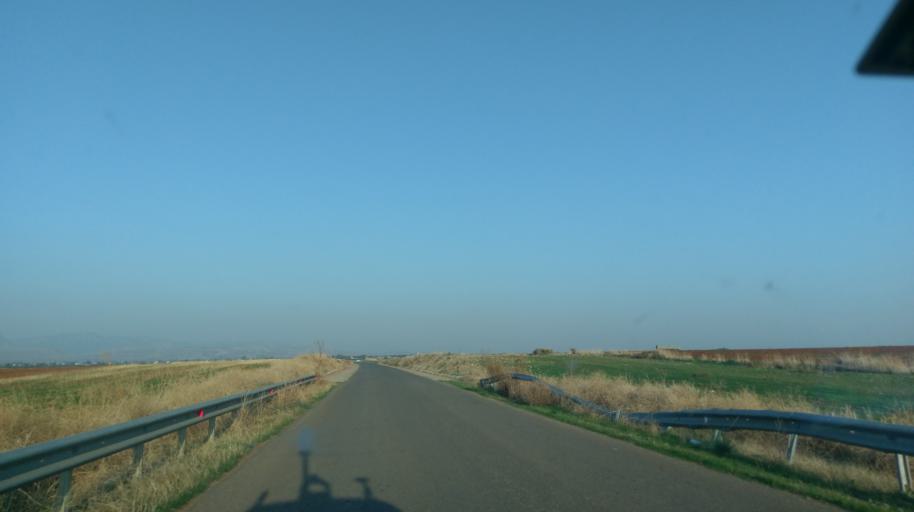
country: CY
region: Lefkosia
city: Morfou
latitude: 35.1469
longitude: 32.9733
